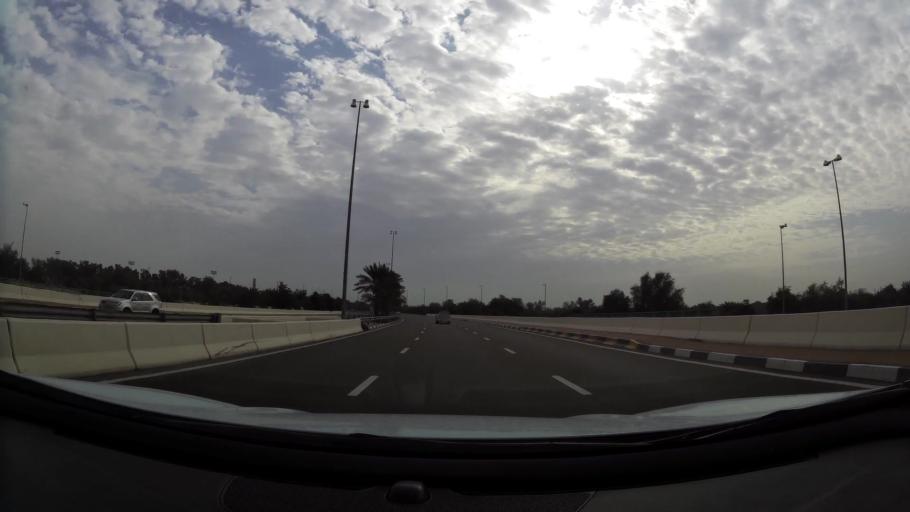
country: AE
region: Abu Dhabi
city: Al Ain
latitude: 24.1763
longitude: 55.6062
